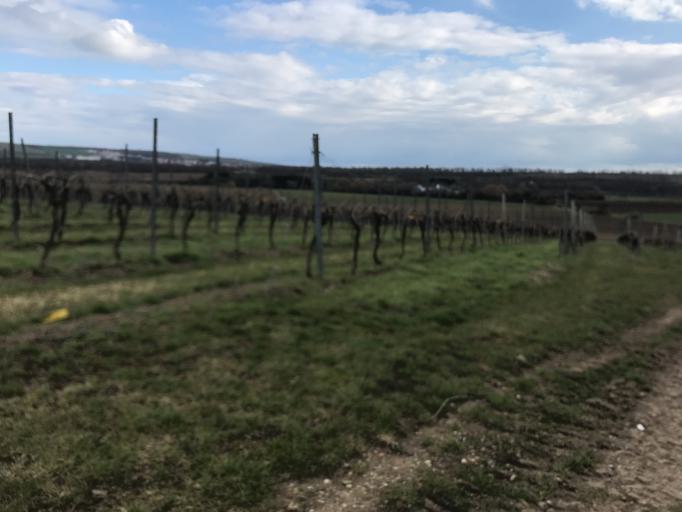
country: DE
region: Rheinland-Pfalz
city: Sorgenloch
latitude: 49.8970
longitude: 8.1726
